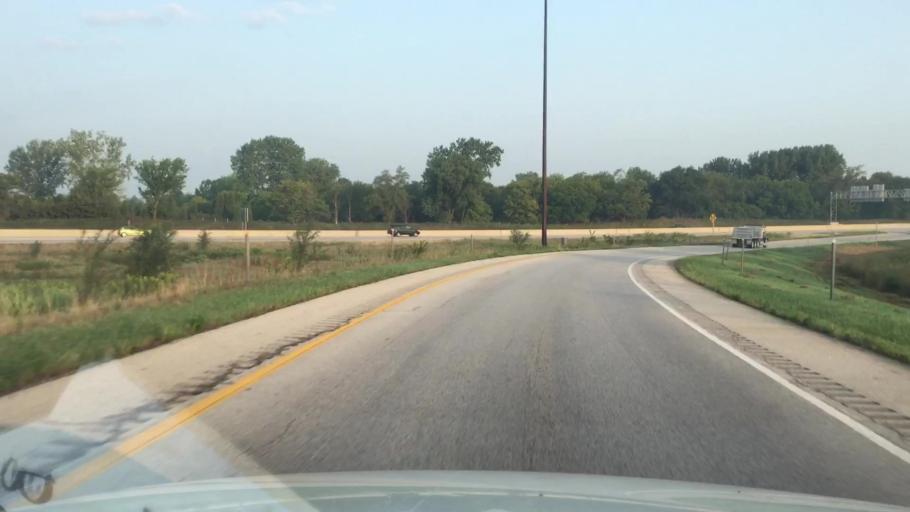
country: US
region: Iowa
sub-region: Polk County
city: Saylorville
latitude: 41.6557
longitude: -93.5741
